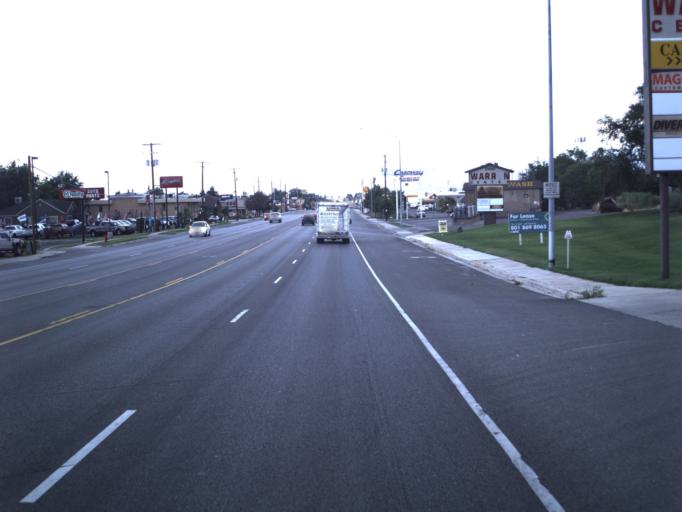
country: US
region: Utah
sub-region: Salt Lake County
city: Sandy City
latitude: 40.6018
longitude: -111.8907
